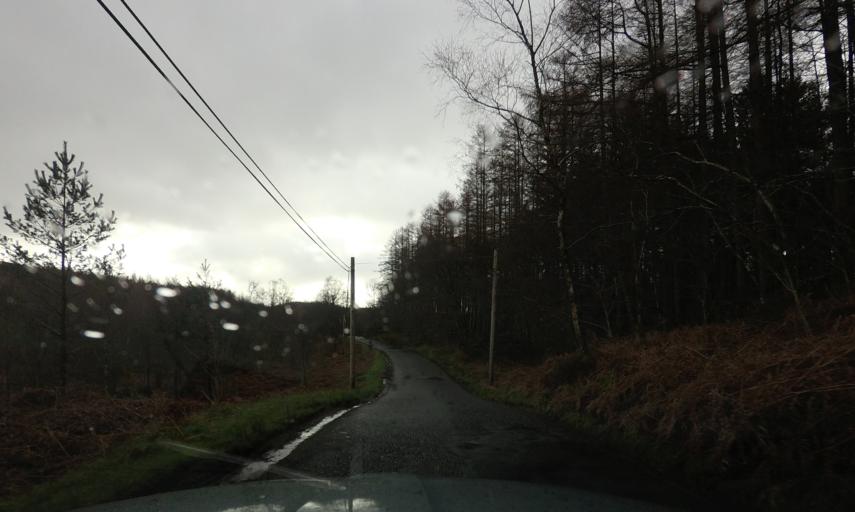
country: GB
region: Scotland
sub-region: West Dunbartonshire
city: Balloch
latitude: 56.1437
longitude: -4.6370
